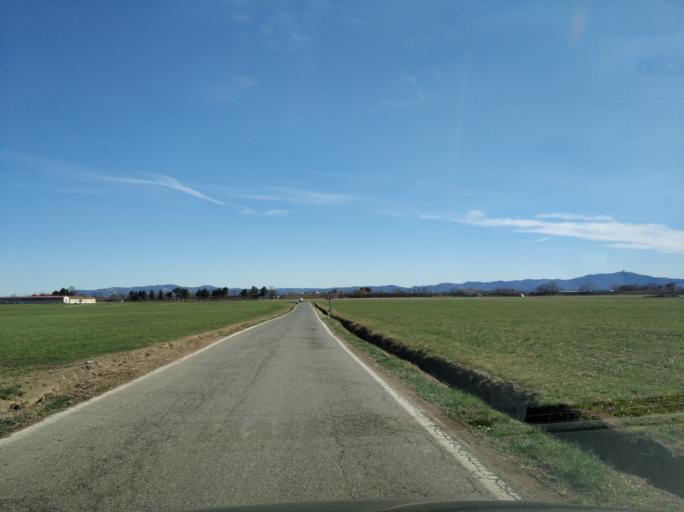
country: IT
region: Piedmont
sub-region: Provincia di Torino
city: Leini
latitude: 45.1941
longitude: 7.6867
